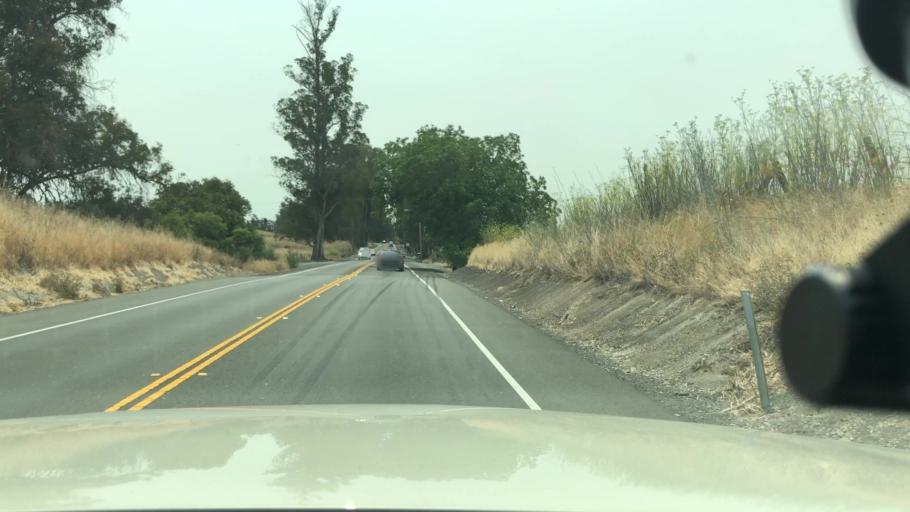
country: US
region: California
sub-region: Marin County
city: Black Point-Green Point
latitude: 38.1864
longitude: -122.5397
